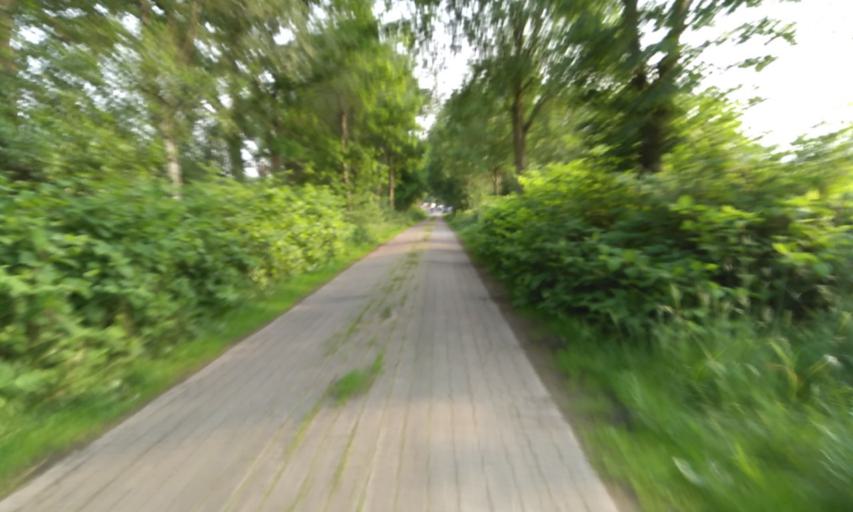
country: DE
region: Lower Saxony
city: Agathenburg
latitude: 53.5263
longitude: 9.4888
